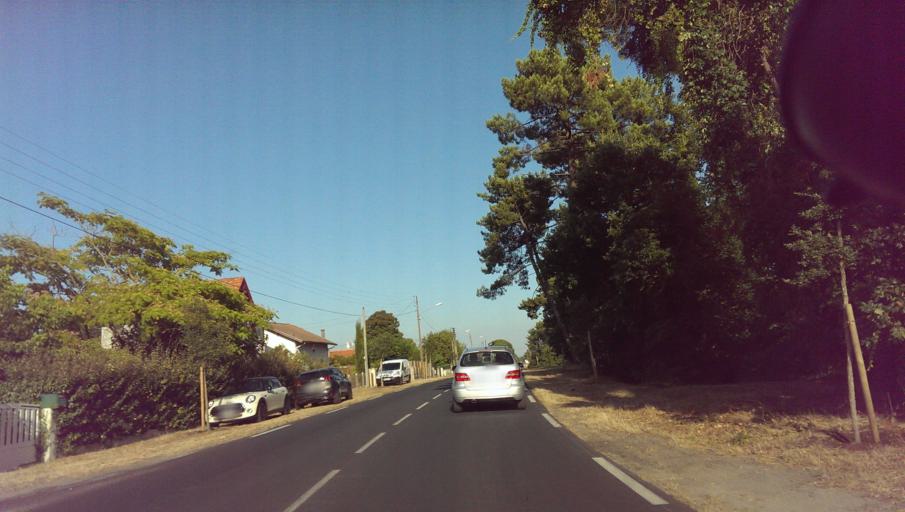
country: FR
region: Aquitaine
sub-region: Departement des Landes
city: Mimizan
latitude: 44.2118
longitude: -1.2658
